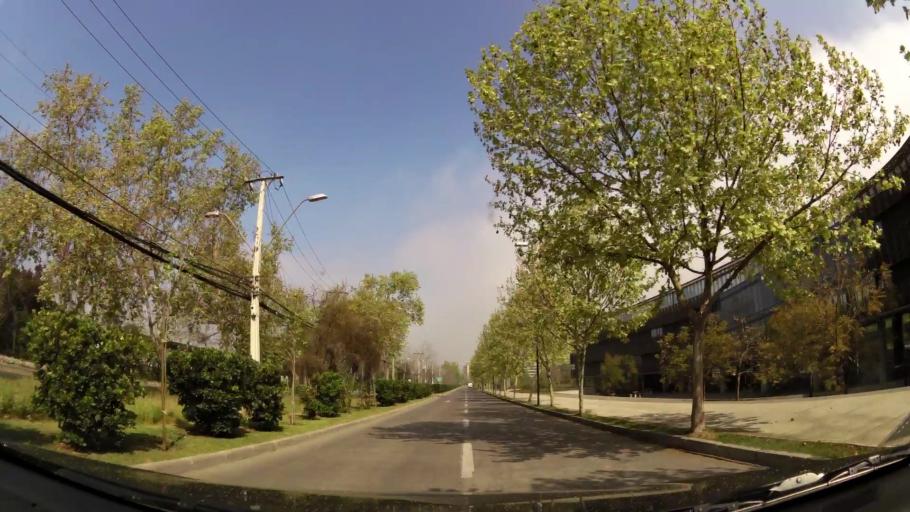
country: CL
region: Santiago Metropolitan
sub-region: Provincia de Santiago
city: Villa Presidente Frei, Nunoa, Santiago, Chile
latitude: -33.3799
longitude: -70.5839
